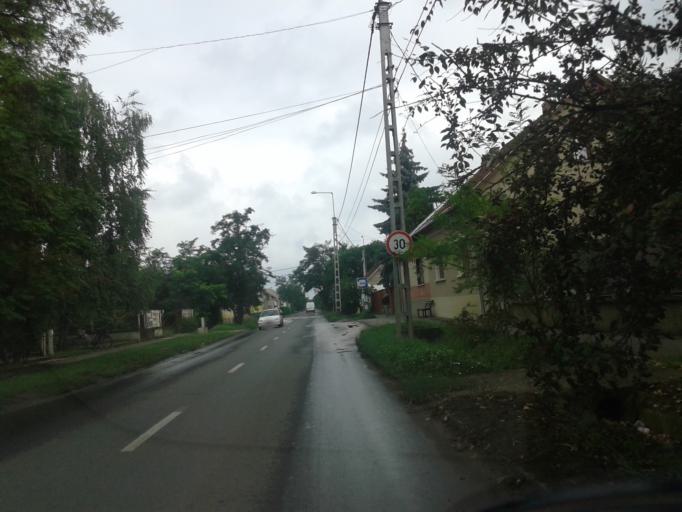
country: HU
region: Csongrad
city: Szeged
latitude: 46.2678
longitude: 20.1776
